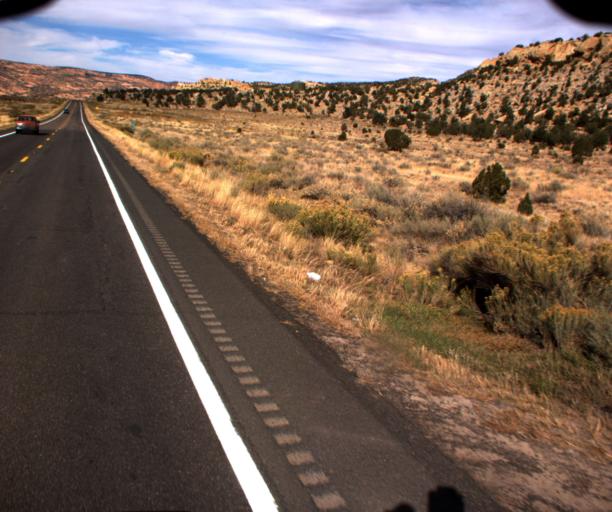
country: US
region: Arizona
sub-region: Navajo County
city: Kayenta
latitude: 36.5876
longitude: -110.4719
